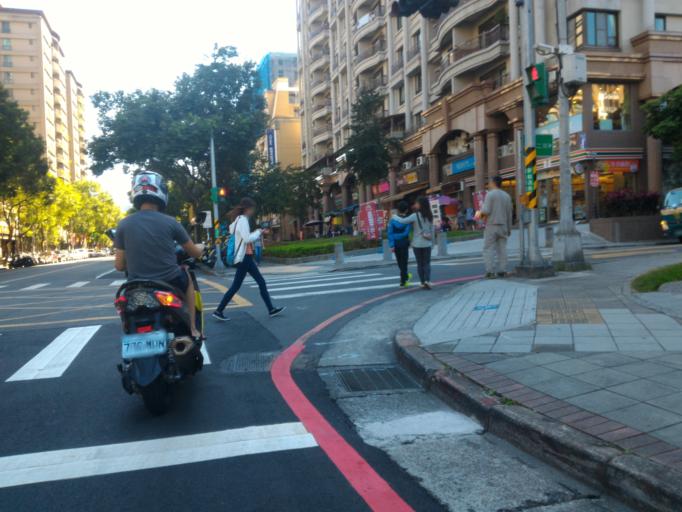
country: TW
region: Taiwan
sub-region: Taoyuan
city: Taoyuan
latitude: 24.9443
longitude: 121.3742
